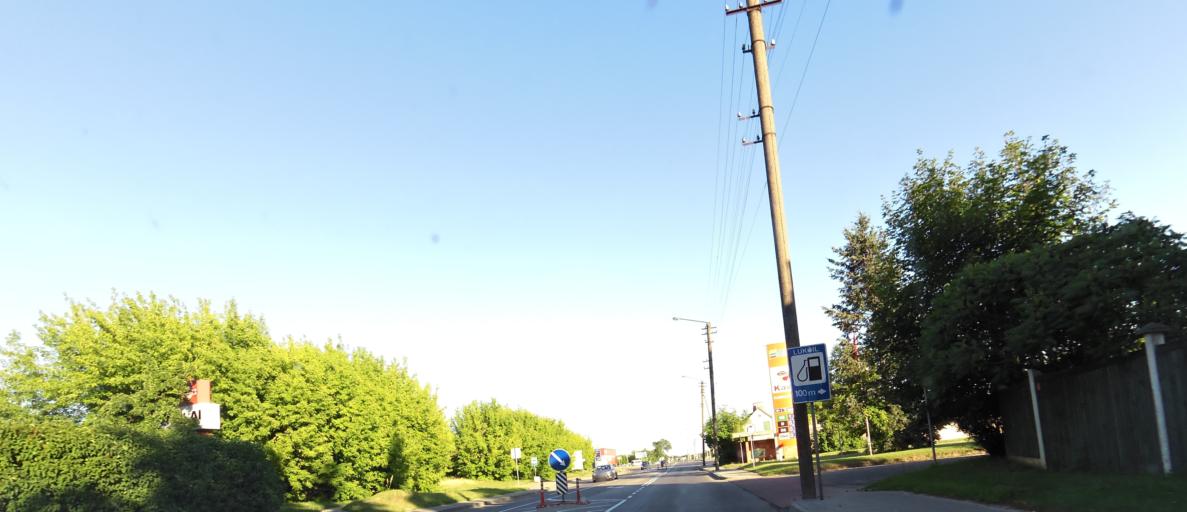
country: LT
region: Panevezys
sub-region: Panevezys City
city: Panevezys
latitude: 55.7107
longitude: 24.3728
